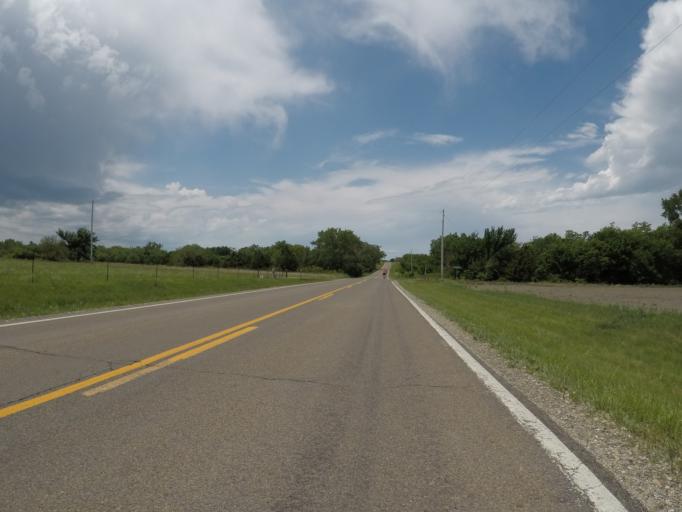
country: US
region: Kansas
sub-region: Morris County
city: Council Grove
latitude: 38.8545
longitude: -96.4273
